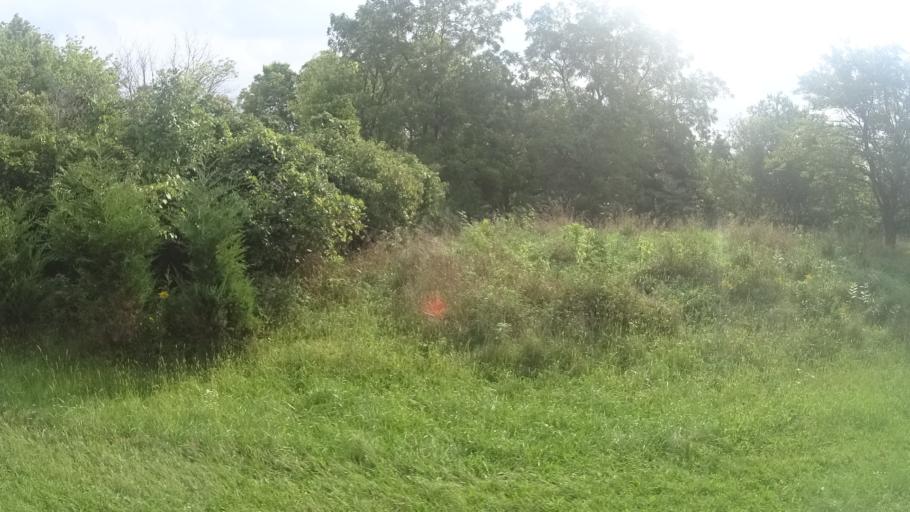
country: US
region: Ohio
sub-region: Erie County
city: Sandusky
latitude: 41.5953
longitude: -82.6960
